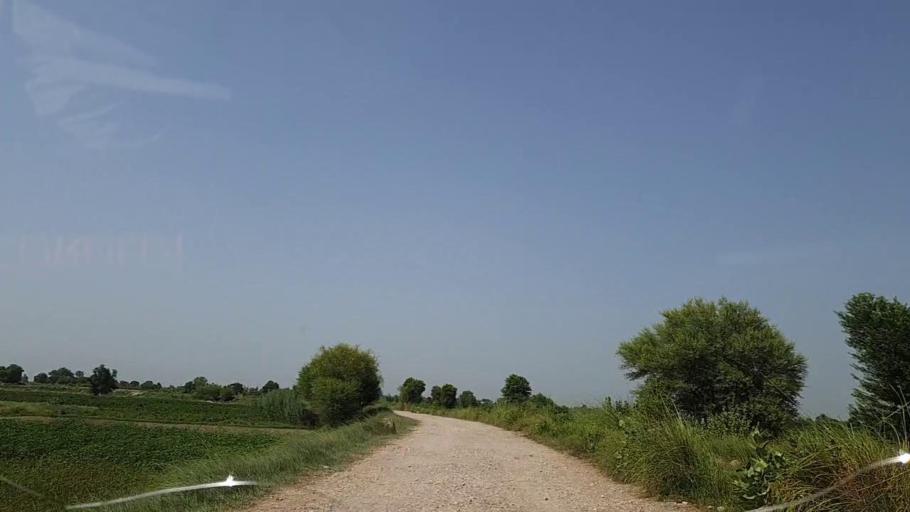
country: PK
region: Sindh
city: Kandiaro
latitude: 27.0459
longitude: 68.1649
